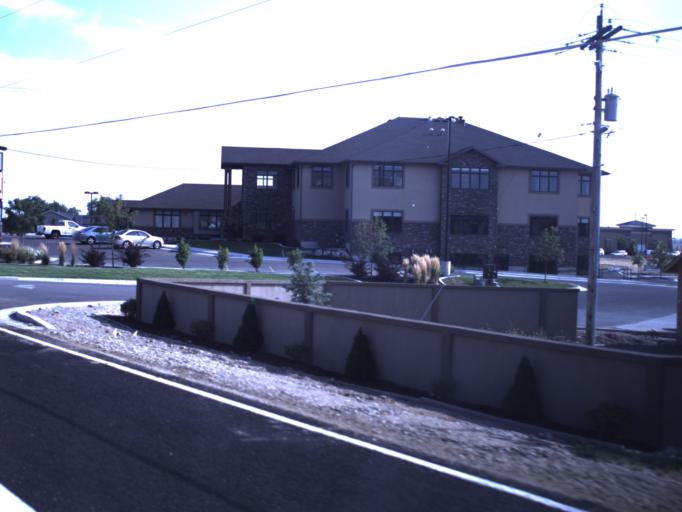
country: US
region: Utah
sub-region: Weber County
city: Pleasant View
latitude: 41.3099
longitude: -112.0083
